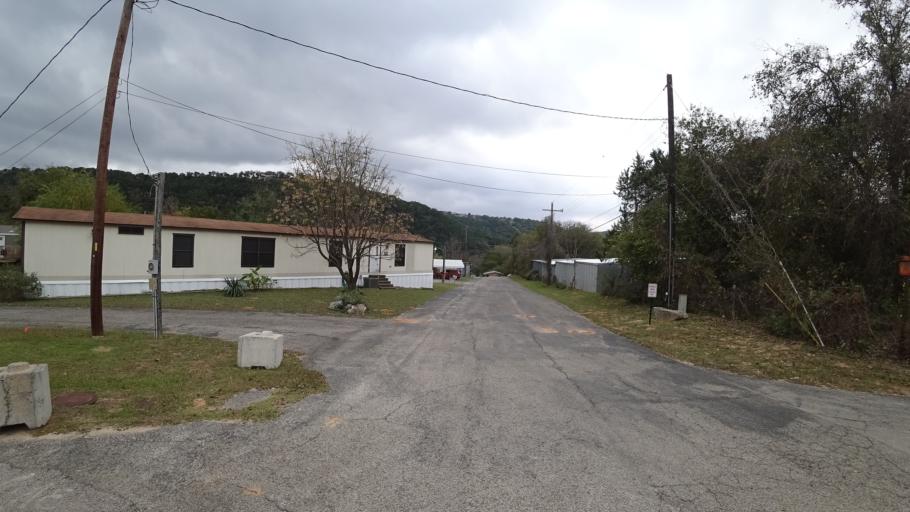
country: US
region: Texas
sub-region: Travis County
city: Bee Cave
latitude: 30.3287
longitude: -97.9193
